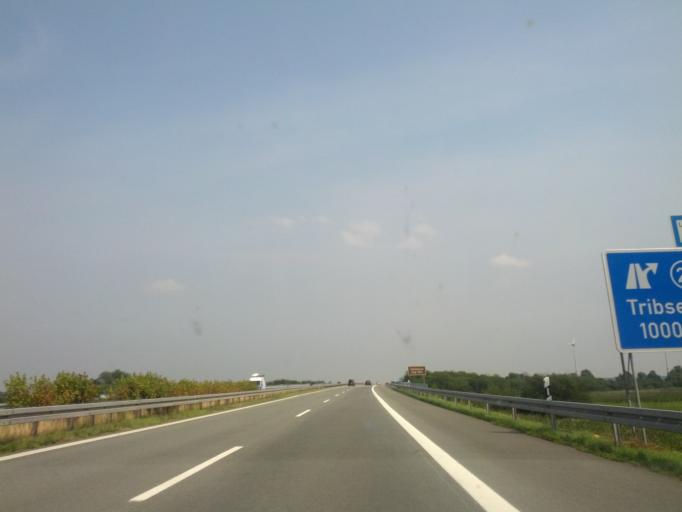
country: DE
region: Mecklenburg-Vorpommern
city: Tribsees
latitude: 54.0763
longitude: 12.7375
